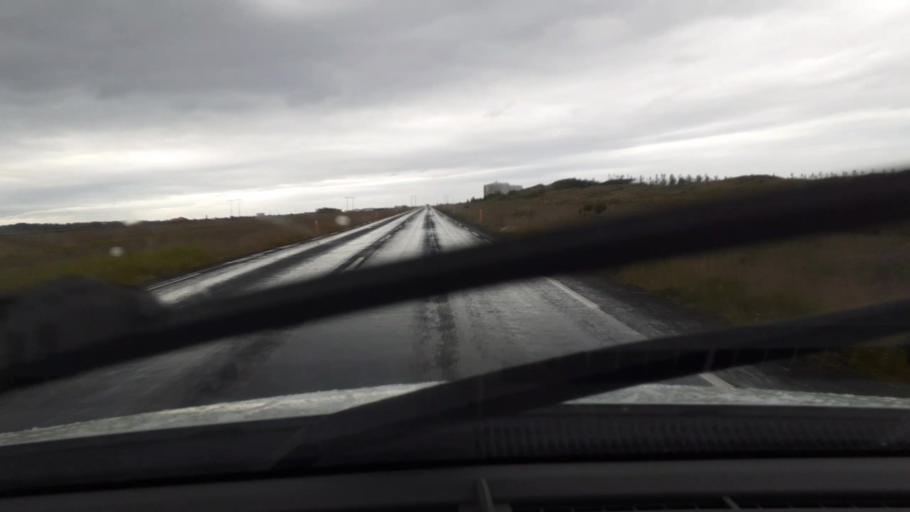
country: IS
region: West
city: Akranes
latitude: 64.3357
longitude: -22.0287
